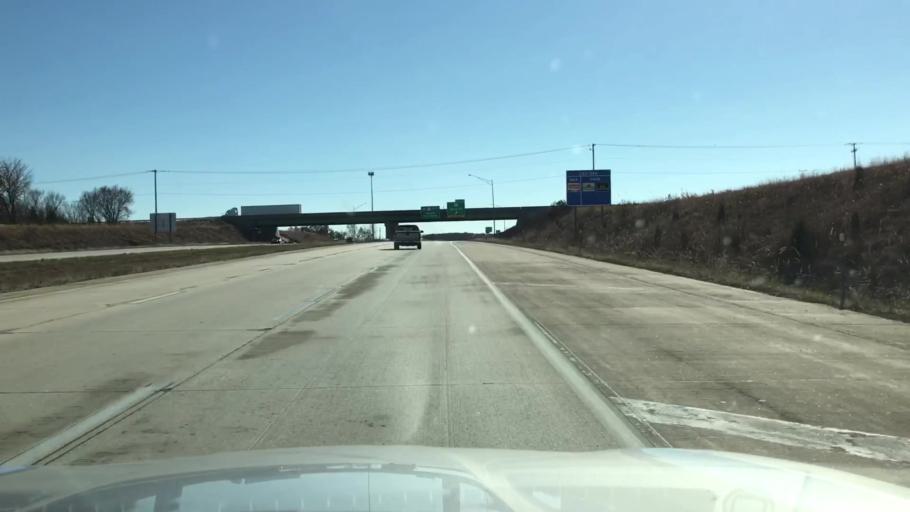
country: US
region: Missouri
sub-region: Jasper County
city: Duenweg
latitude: 37.0565
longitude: -94.4267
